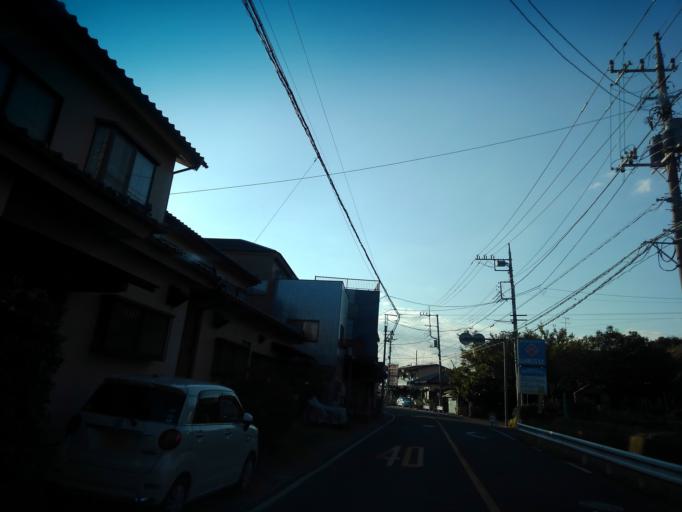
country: JP
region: Saitama
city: Tokorozawa
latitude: 35.7779
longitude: 139.4288
